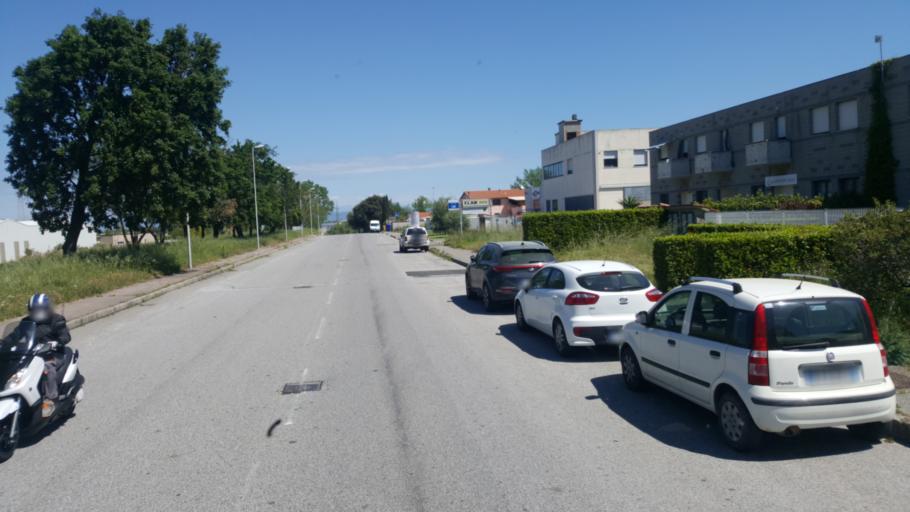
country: IT
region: Tuscany
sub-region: Provincia di Livorno
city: Livorno
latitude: 43.5728
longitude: 10.3434
